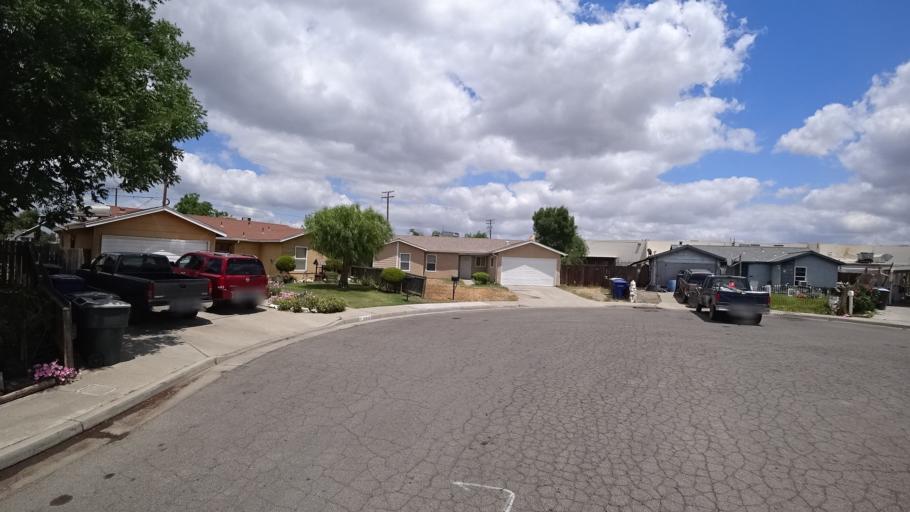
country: US
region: California
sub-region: Kings County
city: Hanford
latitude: 36.3129
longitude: -119.6522
